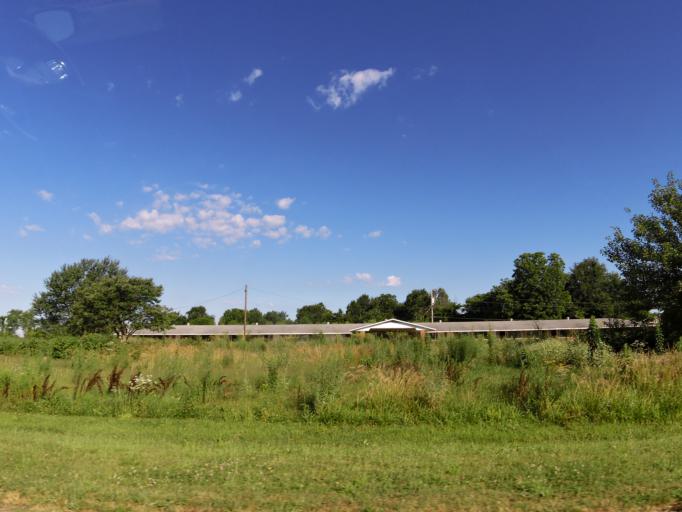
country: US
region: Arkansas
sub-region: Clay County
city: Corning
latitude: 36.5459
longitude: -90.5229
